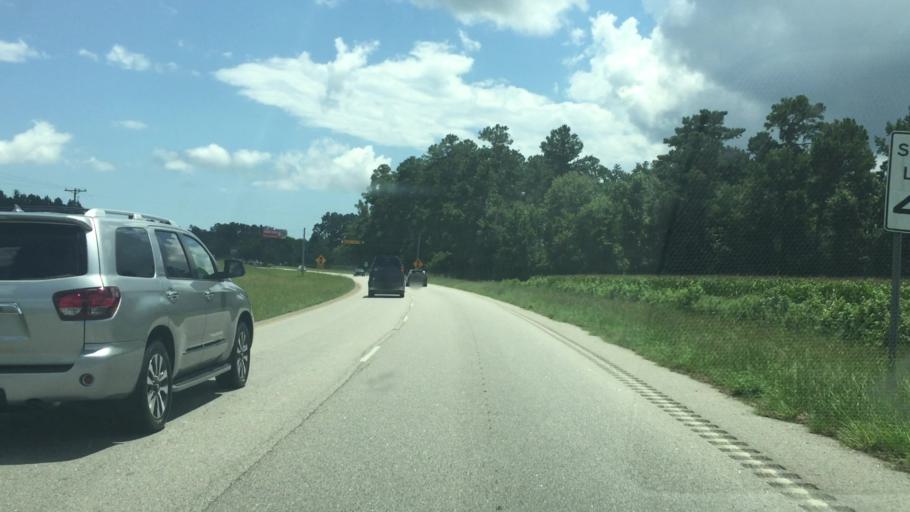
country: US
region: South Carolina
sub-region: Horry County
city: North Myrtle Beach
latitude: 33.9426
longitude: -78.7355
